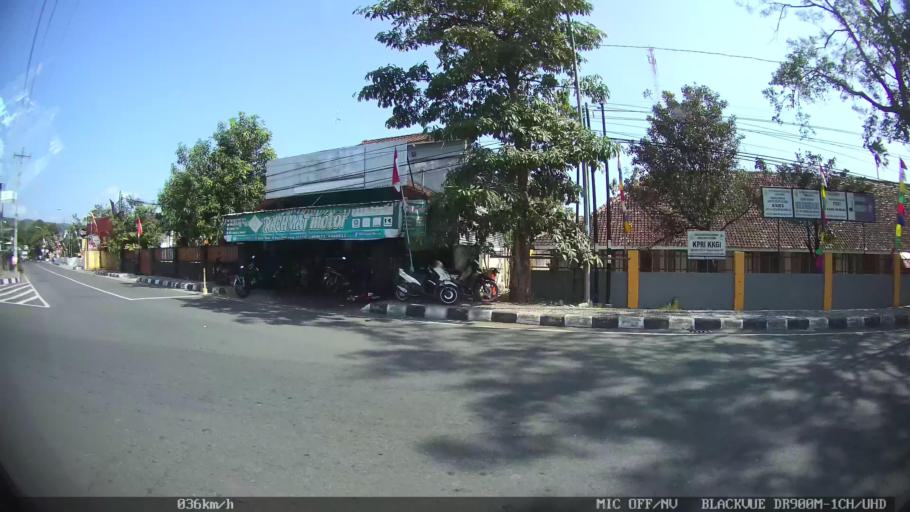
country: ID
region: Daerah Istimewa Yogyakarta
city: Pundong
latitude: -7.9201
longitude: 110.3810
